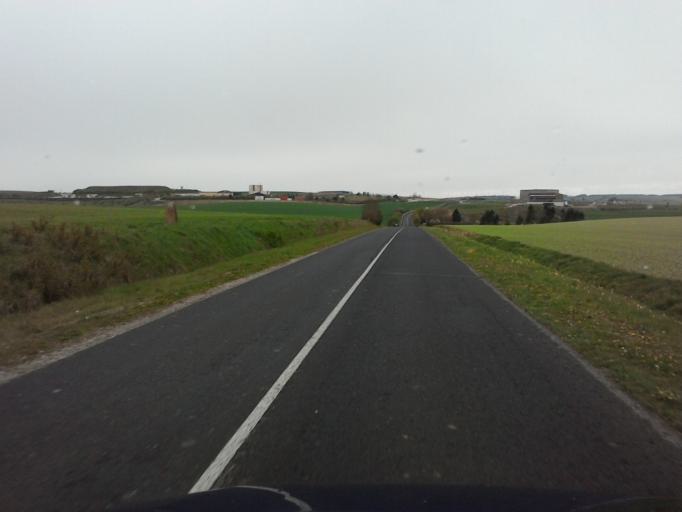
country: FR
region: Lorraine
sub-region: Departement de la Meuse
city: Gondrecourt-le-Chateau
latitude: 48.4886
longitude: 5.3656
